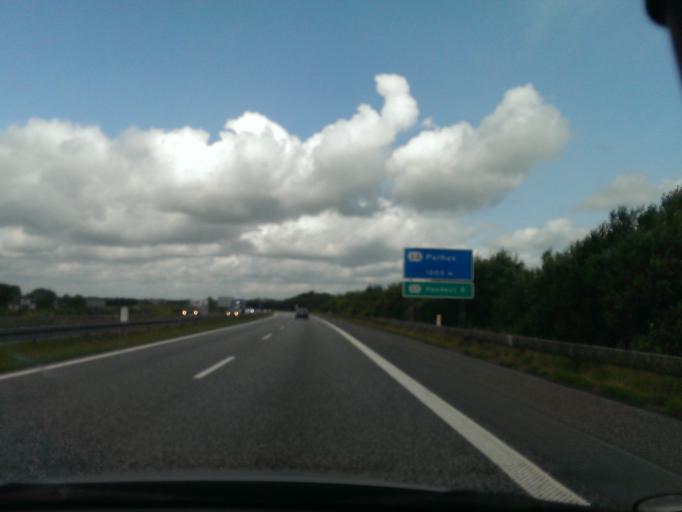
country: DK
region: Central Jutland
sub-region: Randers Kommune
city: Spentrup
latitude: 56.5355
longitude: 9.9230
